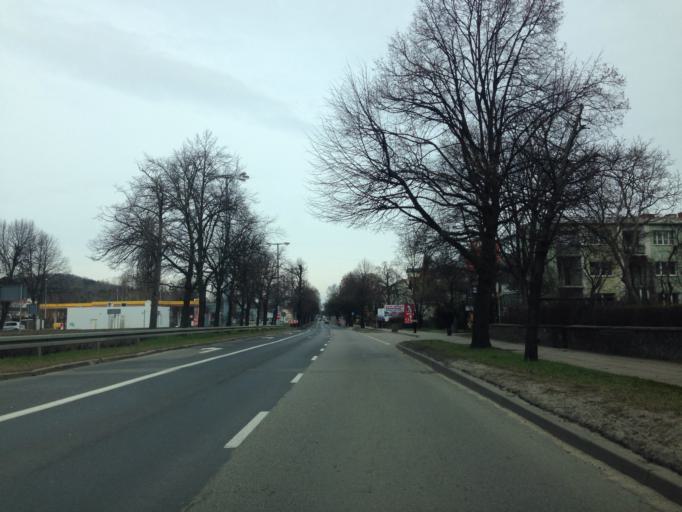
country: PL
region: Pomeranian Voivodeship
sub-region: Sopot
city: Sopot
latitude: 54.4147
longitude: 18.5665
